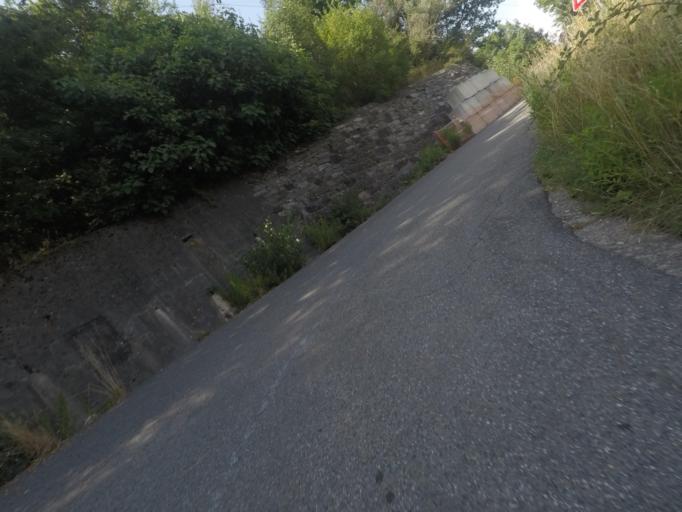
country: IT
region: Tuscany
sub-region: Provincia di Massa-Carrara
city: Fivizzano
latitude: 44.1699
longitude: 10.1078
